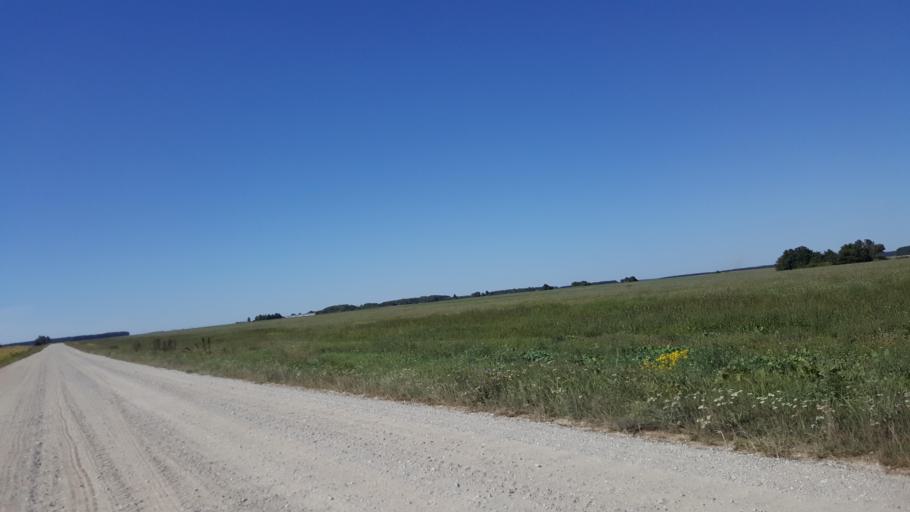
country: PL
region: Lublin Voivodeship
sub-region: Powiat bialski
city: Rokitno
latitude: 52.2285
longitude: 23.3250
